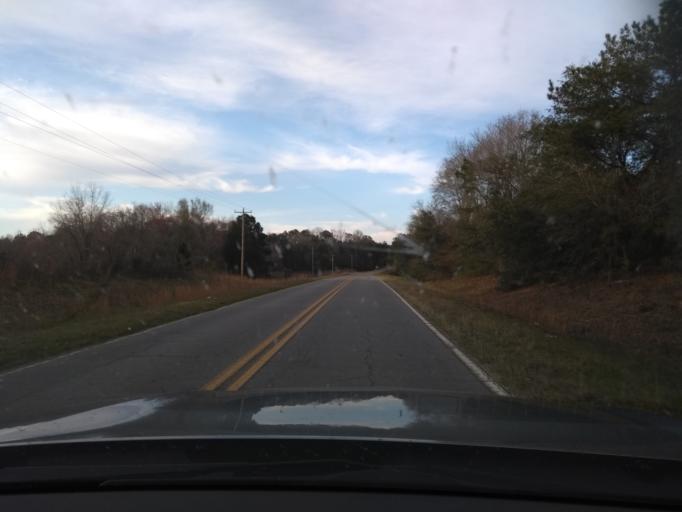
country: US
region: Georgia
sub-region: Evans County
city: Claxton
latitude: 32.2139
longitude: -81.7684
